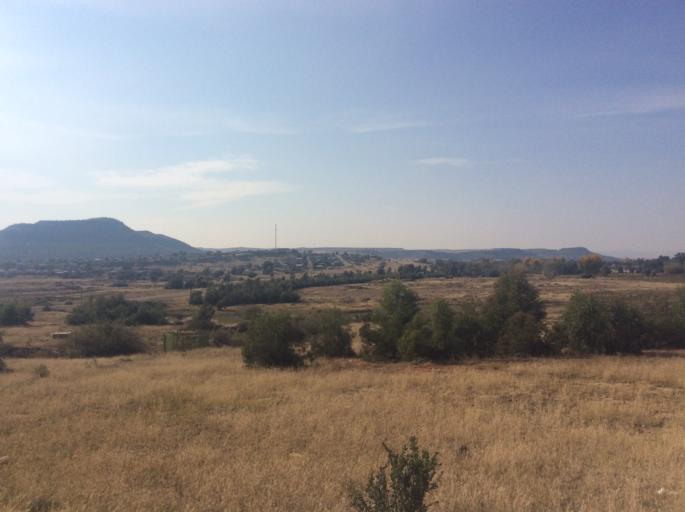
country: LS
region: Mafeteng
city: Mafeteng
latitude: -29.7225
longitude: 27.0179
